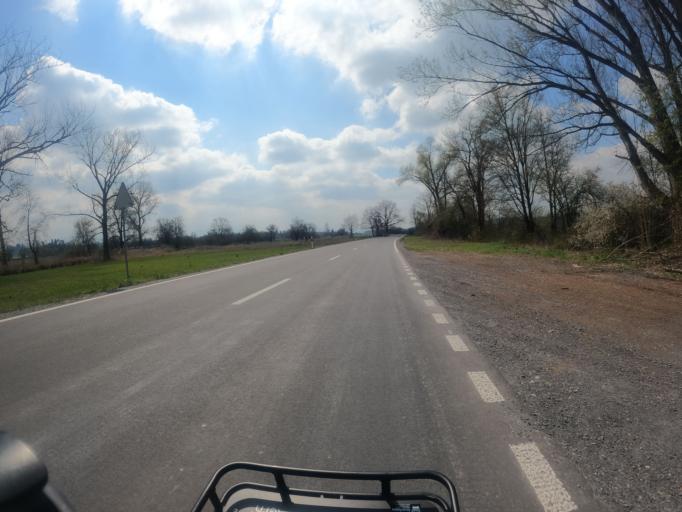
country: CH
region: Zurich
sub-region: Bezirk Affoltern
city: Obfelden / Oberlunnern
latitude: 47.2320
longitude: 8.4163
